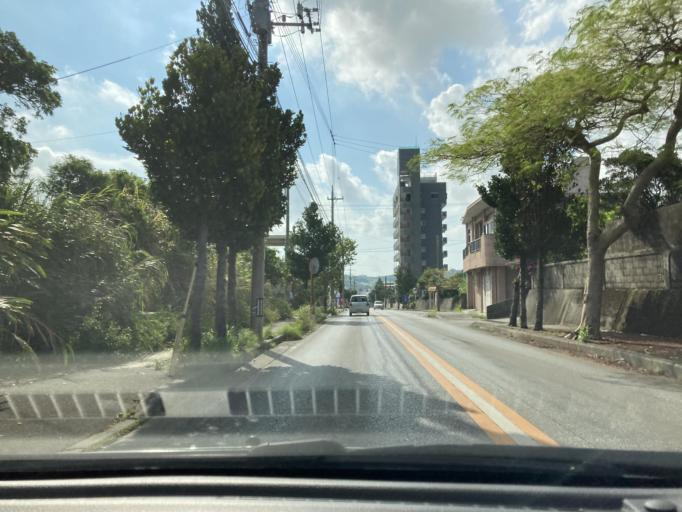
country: JP
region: Okinawa
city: Tomigusuku
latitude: 26.1601
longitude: 127.7454
